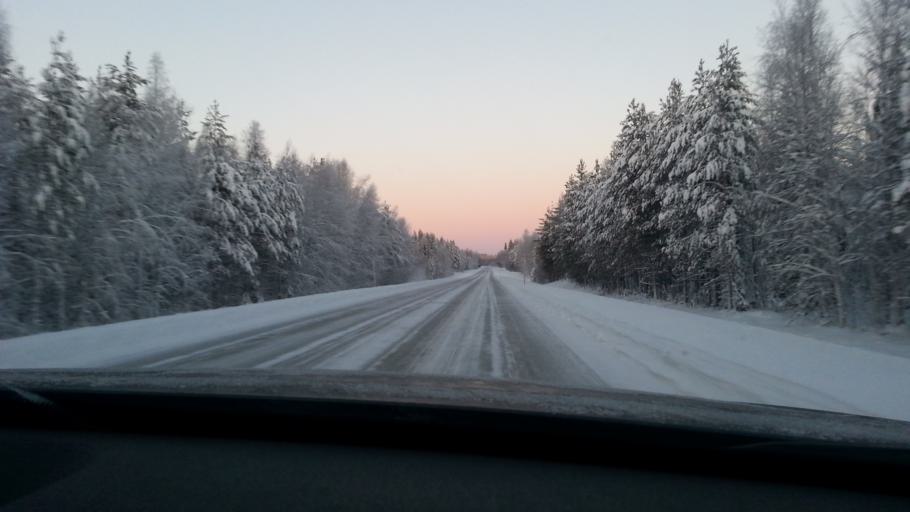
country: FI
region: Lapland
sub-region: Tunturi-Lappi
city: Kittilae
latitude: 67.2237
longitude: 24.9234
